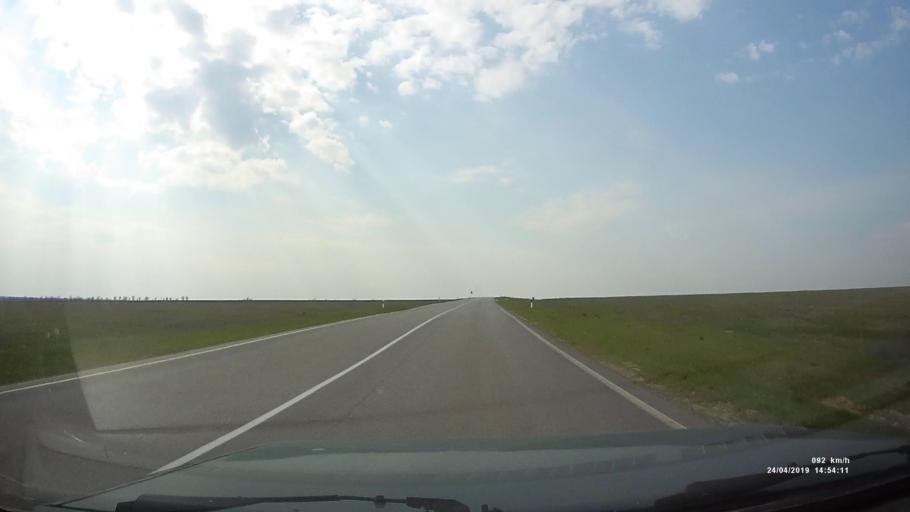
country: RU
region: Rostov
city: Remontnoye
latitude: 46.5329
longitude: 43.6436
